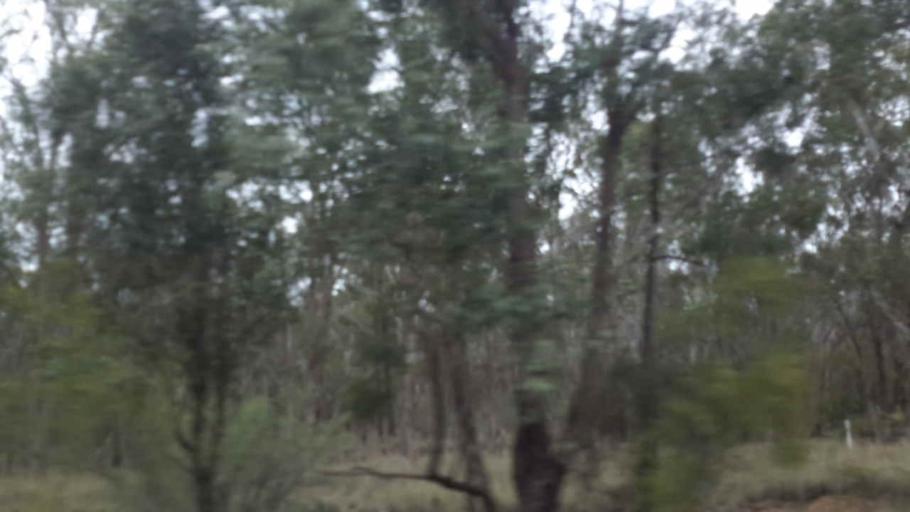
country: AU
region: New South Wales
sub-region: Hawkesbury
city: South Windsor
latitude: -33.6285
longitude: 150.7749
